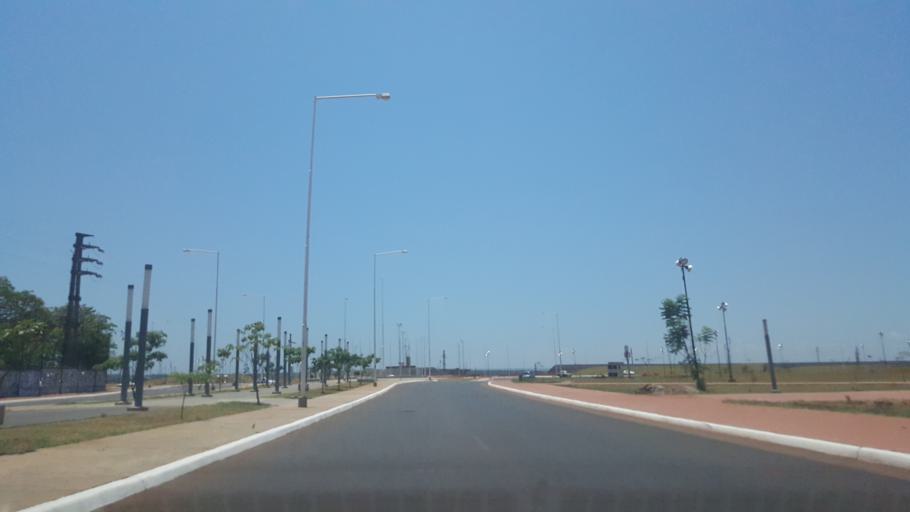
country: AR
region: Misiones
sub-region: Departamento de Capital
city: Posadas
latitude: -27.3755
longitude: -55.8876
